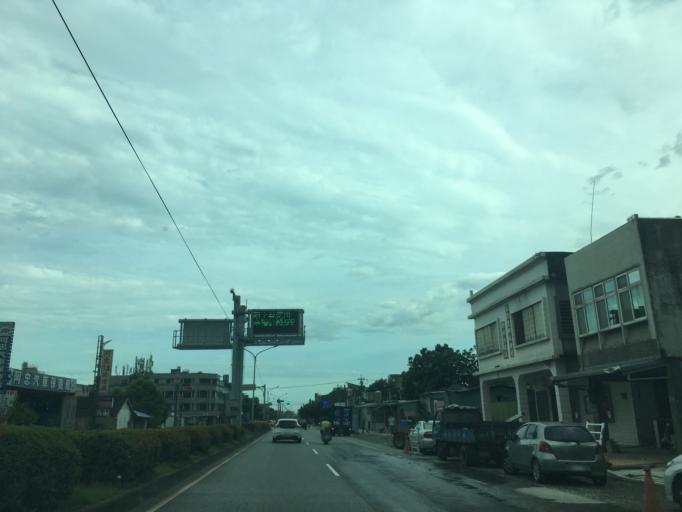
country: TW
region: Taiwan
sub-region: Hualien
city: Hualian
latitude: 24.0382
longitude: 121.6043
